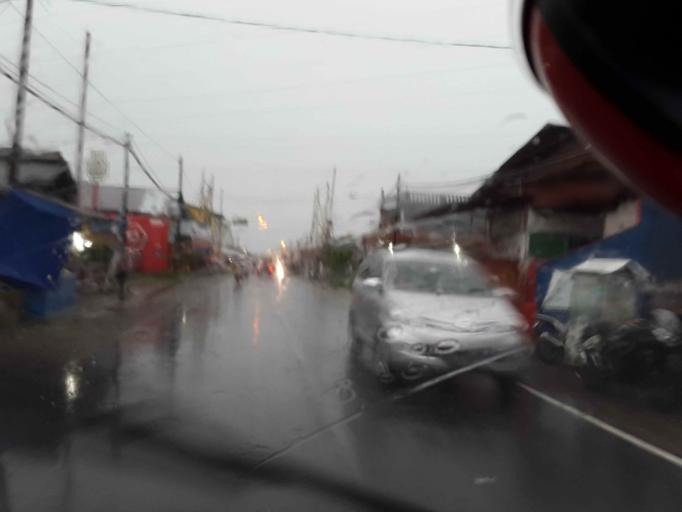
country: ID
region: West Java
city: Cimahi
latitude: -6.9126
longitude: 107.5006
